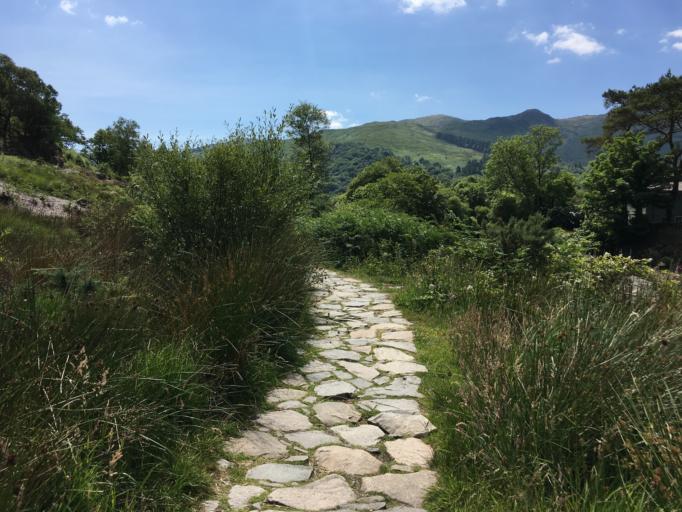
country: GB
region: Wales
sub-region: Gwynedd
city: Penrhyndeudraeth
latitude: 53.0134
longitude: -4.0987
